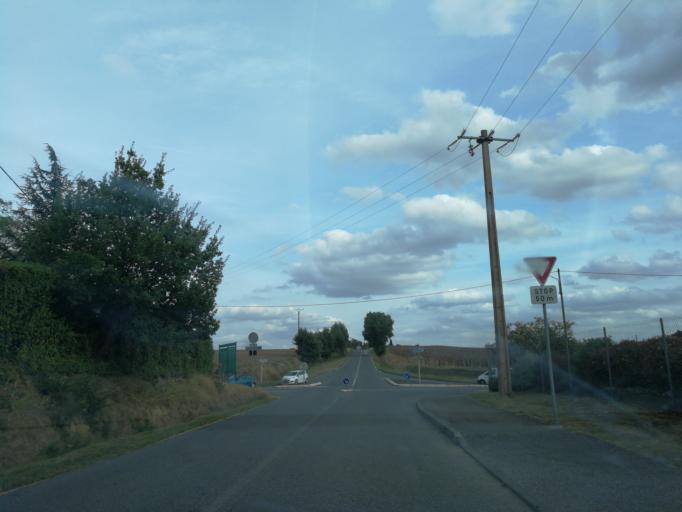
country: FR
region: Midi-Pyrenees
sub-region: Departement de la Haute-Garonne
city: Flourens
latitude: 43.5987
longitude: 1.5477
